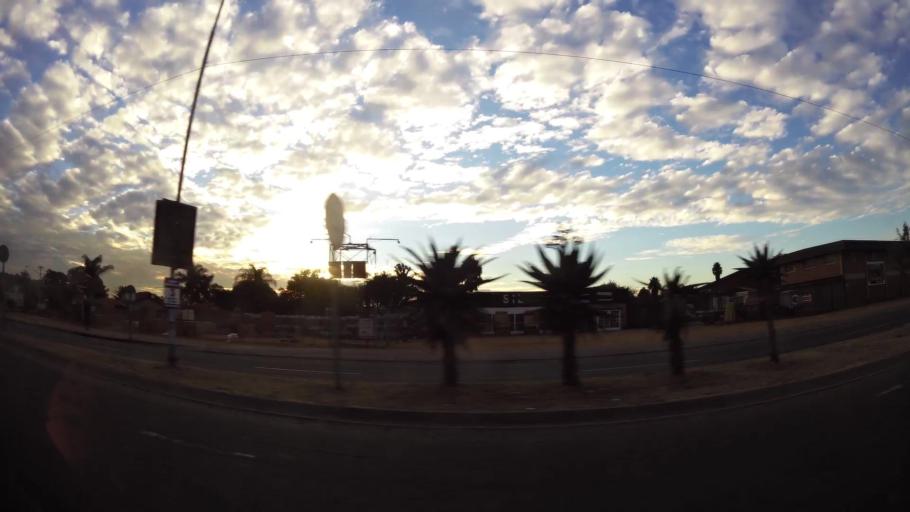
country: ZA
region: Gauteng
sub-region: City of Tshwane Metropolitan Municipality
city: Pretoria
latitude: -25.7338
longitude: 28.3148
